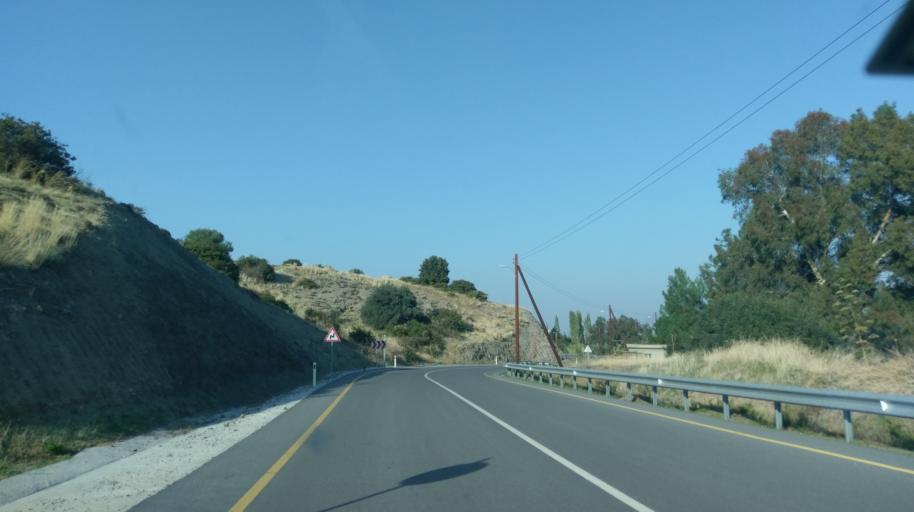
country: CY
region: Lefkosia
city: Lefka
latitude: 35.0860
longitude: 32.8413
